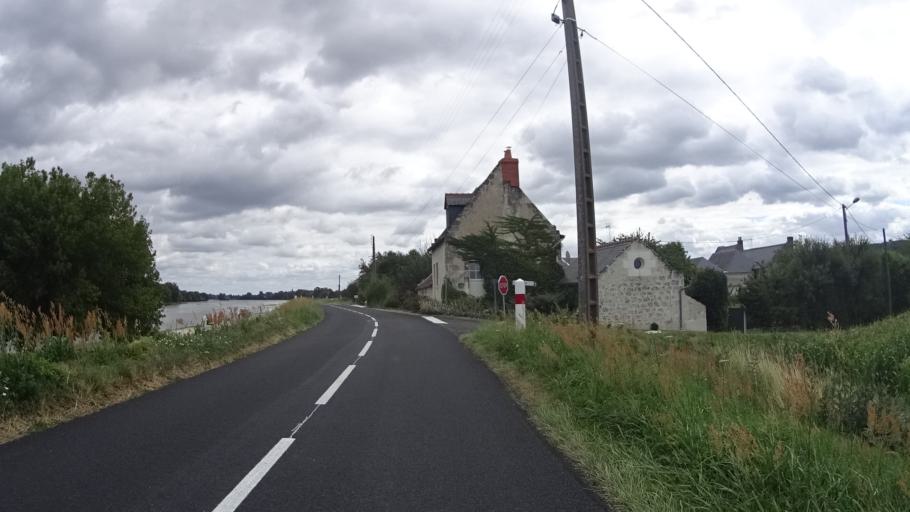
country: FR
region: Centre
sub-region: Departement d'Indre-et-Loire
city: Huismes
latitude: 47.2633
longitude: 0.2974
